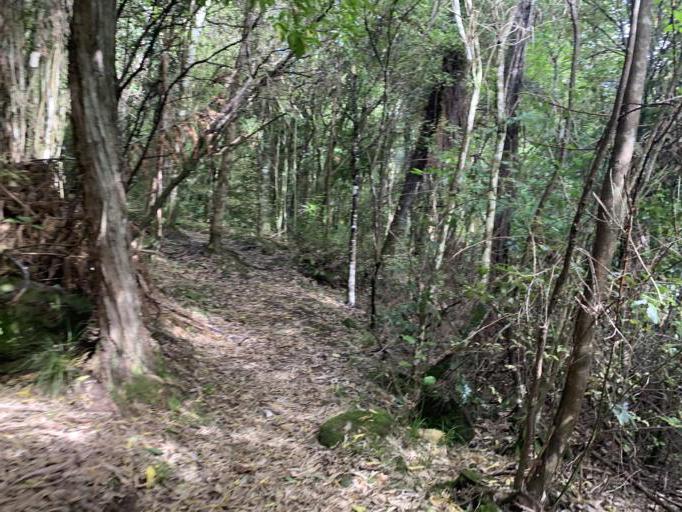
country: NZ
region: Waikato
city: Turangi
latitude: -38.9729
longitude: 175.7753
